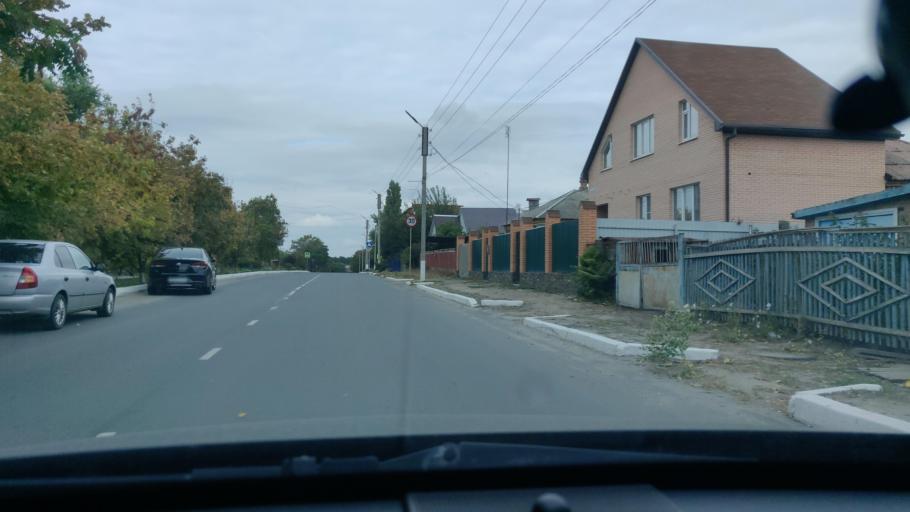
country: RU
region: Rostov
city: Ust'-Donetskiy
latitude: 47.6431
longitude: 40.8651
